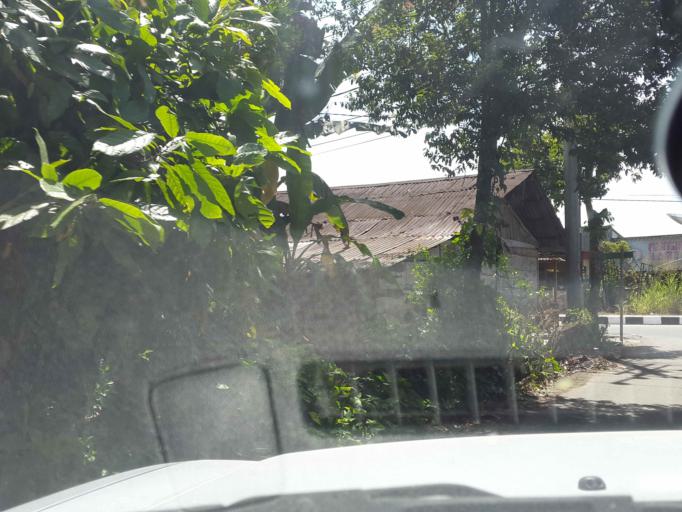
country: ID
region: West Sumatra
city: Bukittinggi
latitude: -0.2899
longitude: 100.3661
